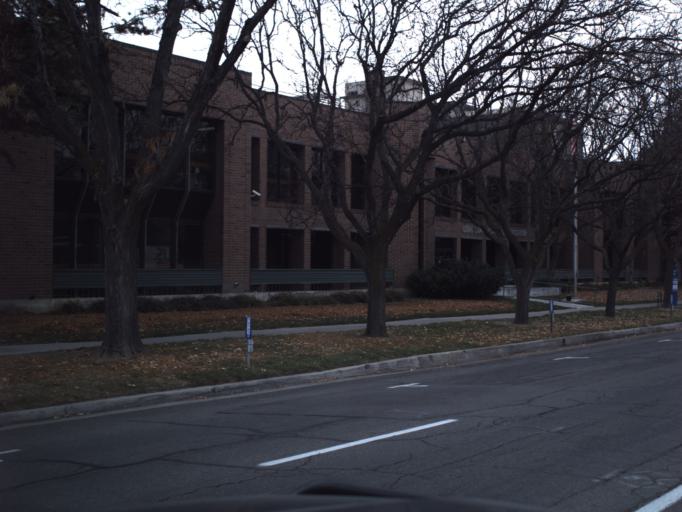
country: US
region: Utah
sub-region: Salt Lake County
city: Salt Lake City
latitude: 40.7585
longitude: -111.8832
